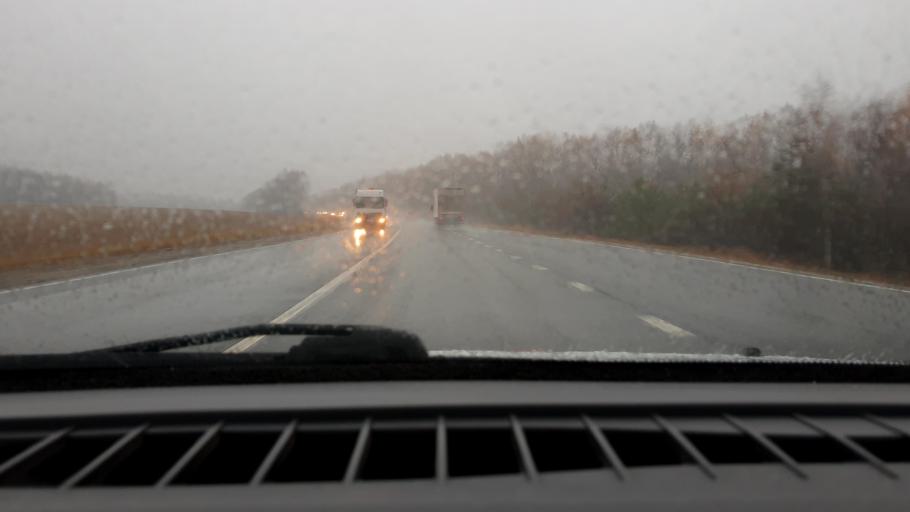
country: RU
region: Nizjnij Novgorod
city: Linda
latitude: 56.5791
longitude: 44.0229
